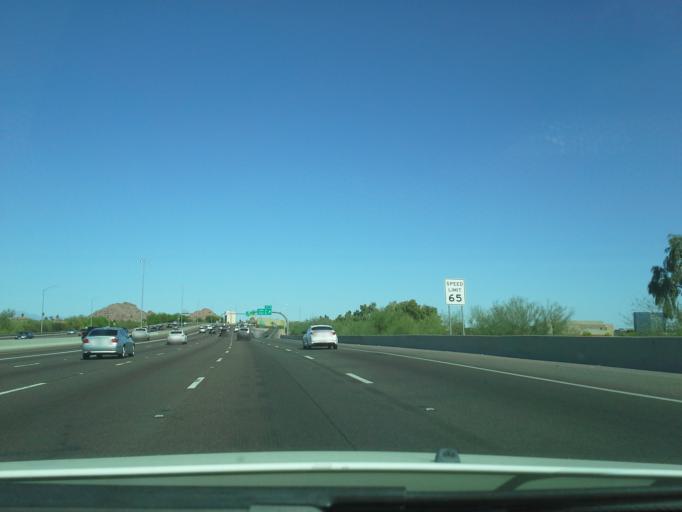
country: US
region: Arizona
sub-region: Maricopa County
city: Phoenix
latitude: 33.4589
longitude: -112.0030
